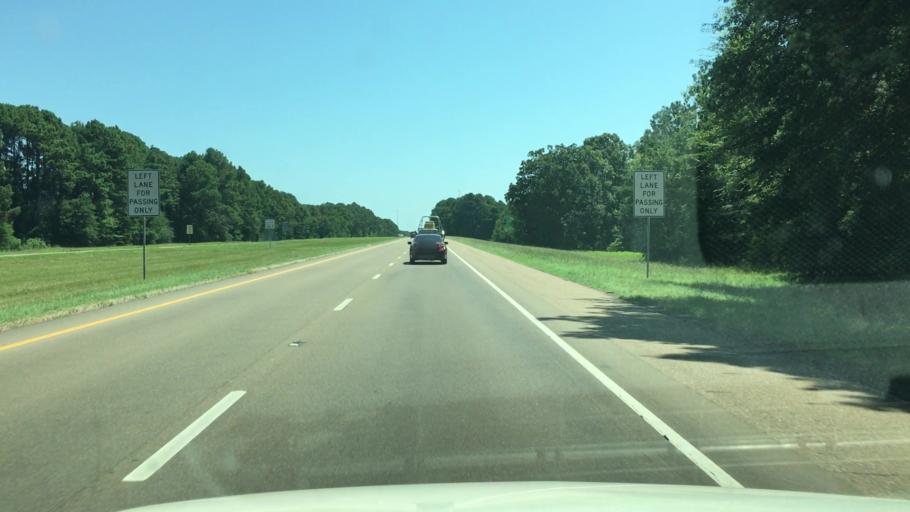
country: US
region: Texas
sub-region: Bowie County
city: New Boston
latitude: 33.4562
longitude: -94.4893
